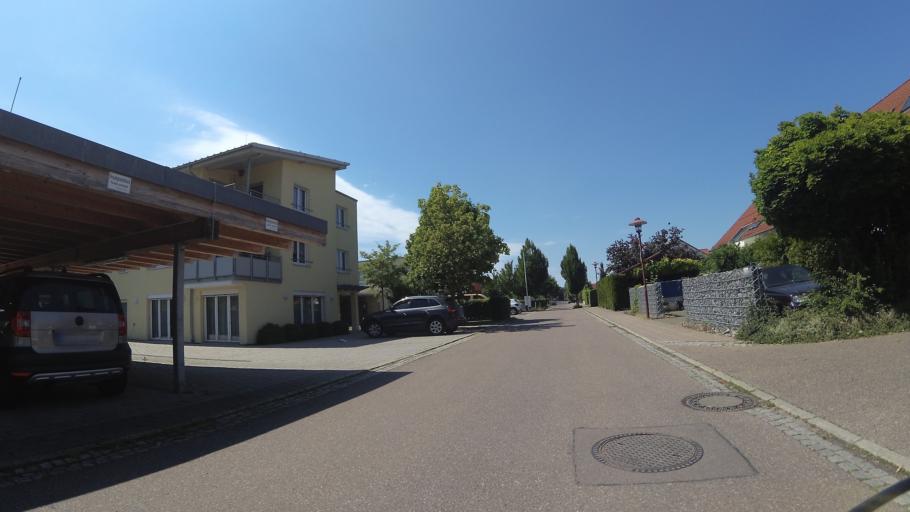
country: DE
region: Baden-Wuerttemberg
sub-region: Regierungsbezirk Stuttgart
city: Erlenbach
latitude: 49.1698
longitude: 9.2667
